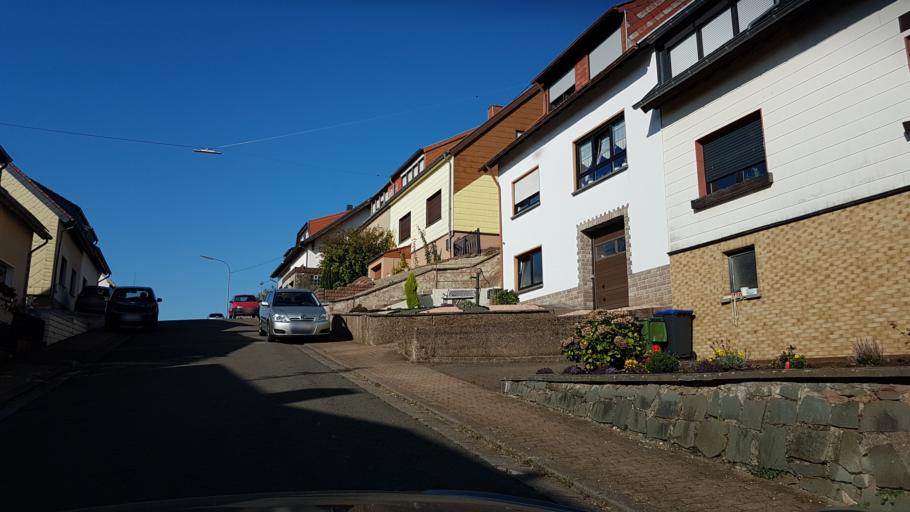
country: DE
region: Saarland
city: Eppelborn
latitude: 49.3993
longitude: 6.9875
